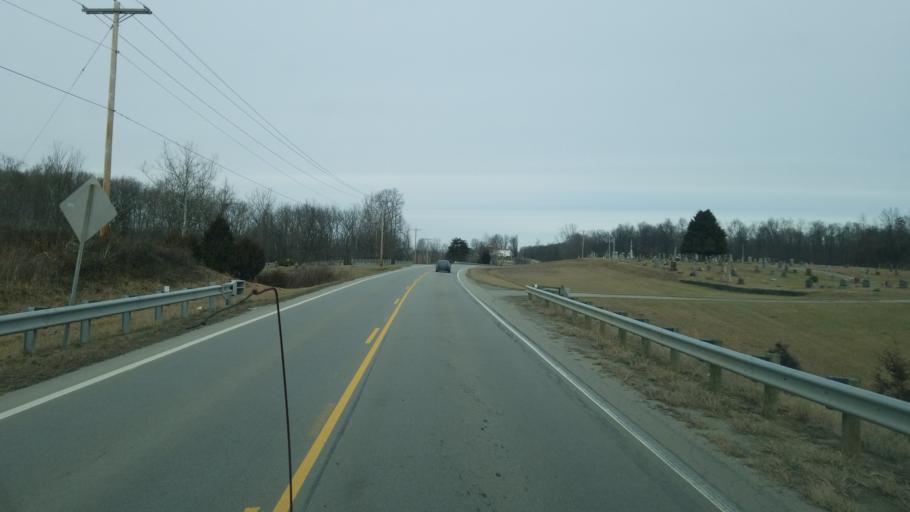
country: US
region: Ohio
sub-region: Adams County
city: Winchester
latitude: 38.9982
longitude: -83.7125
